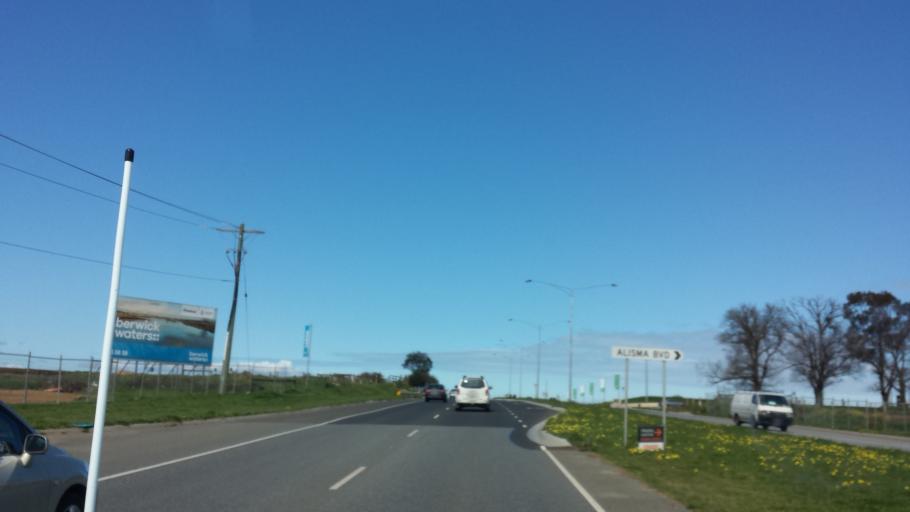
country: AU
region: Victoria
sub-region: Casey
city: Berwick
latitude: -38.0767
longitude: 145.3352
